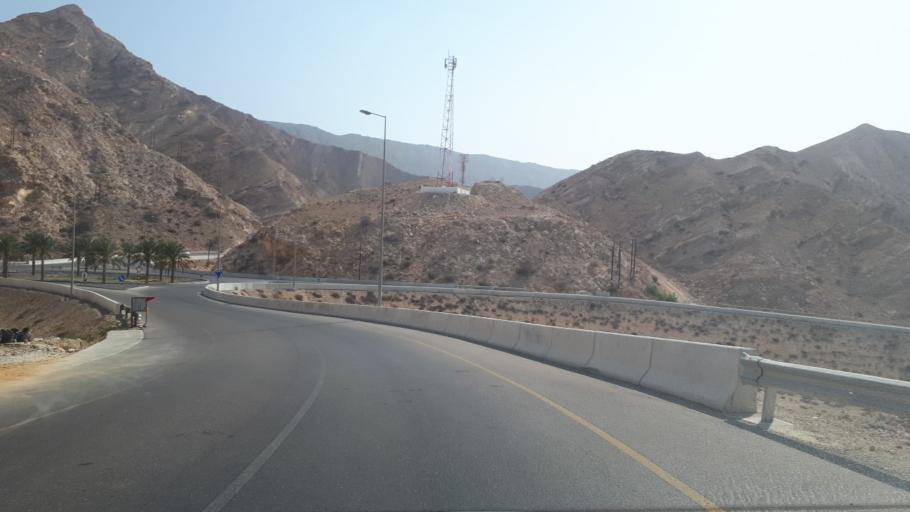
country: OM
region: Muhafazat Masqat
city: Muscat
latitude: 23.5426
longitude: 58.6477
